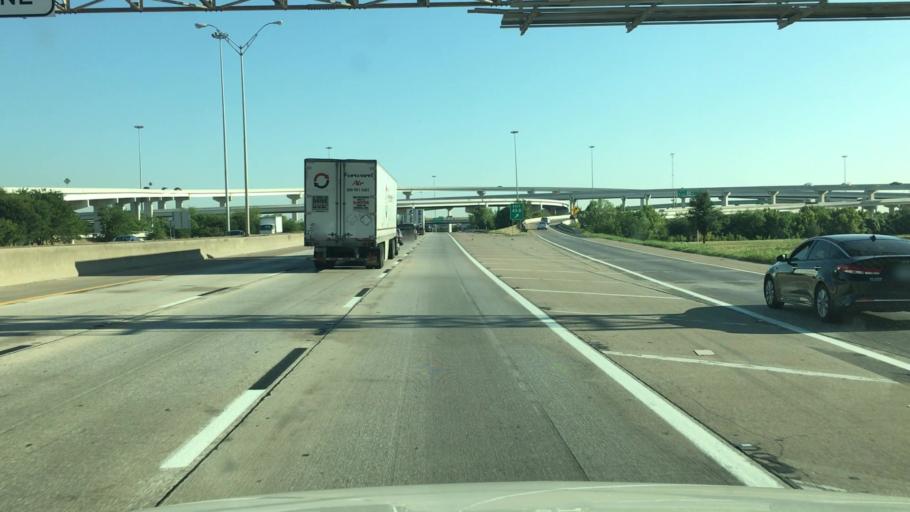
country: US
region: Texas
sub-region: Tarrant County
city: Edgecliff Village
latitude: 32.6628
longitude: -97.3210
